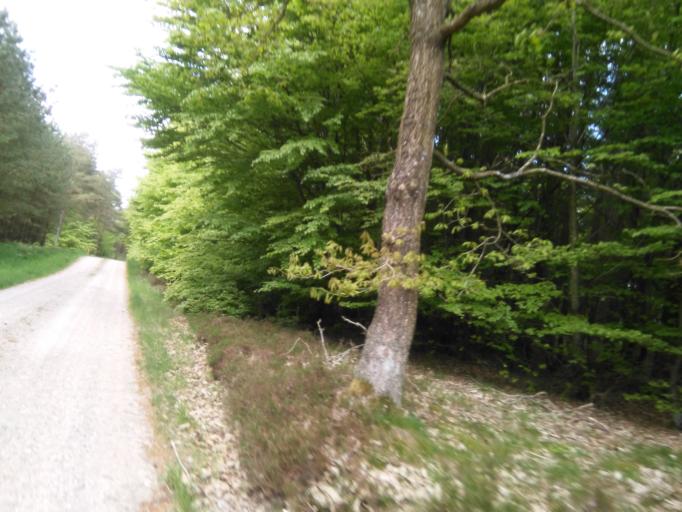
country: DK
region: Central Jutland
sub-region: Silkeborg Kommune
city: Svejbaek
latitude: 56.0622
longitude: 9.6217
